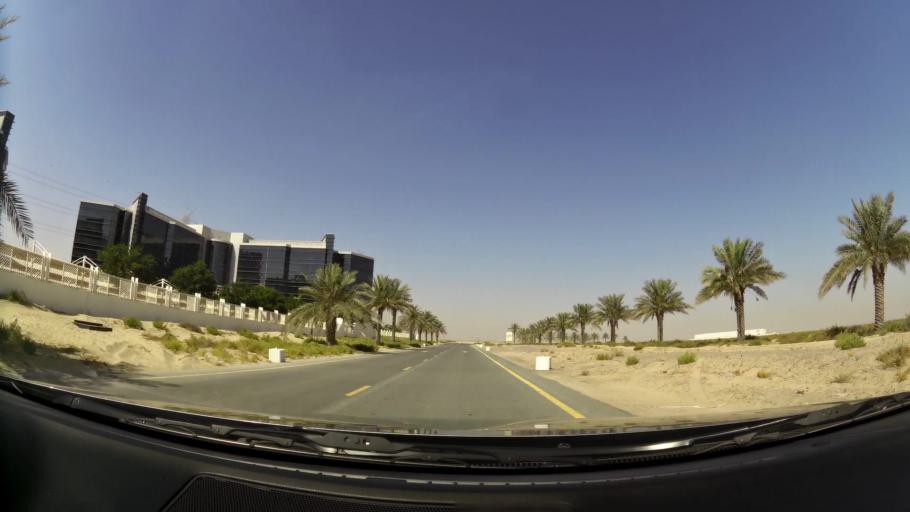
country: AE
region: Dubai
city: Dubai
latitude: 24.8983
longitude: 55.0613
